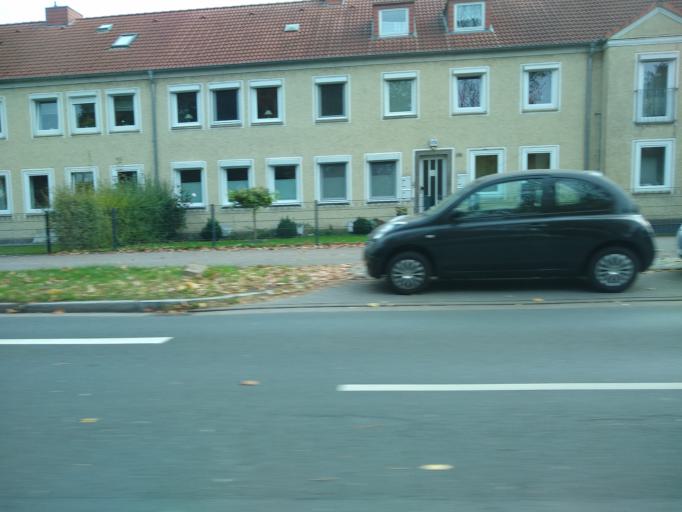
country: DE
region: Lower Saxony
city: Delmenhorst
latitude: 53.0451
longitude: 8.5957
